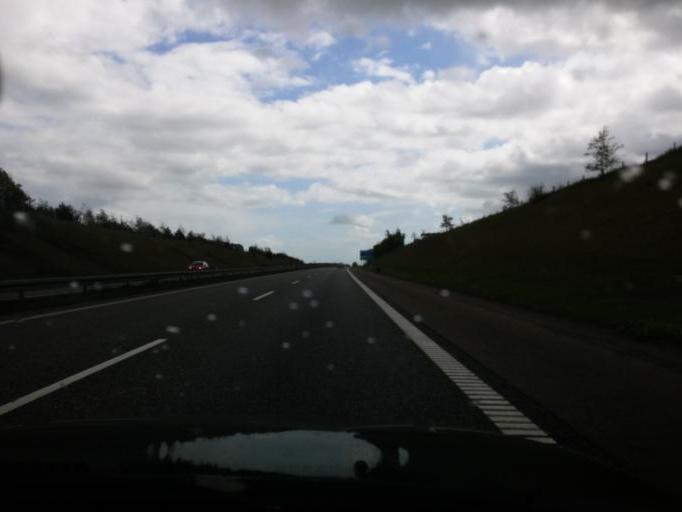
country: DK
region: South Denmark
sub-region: Faaborg-Midtfyn Kommune
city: Arslev
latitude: 55.2759
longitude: 10.4602
